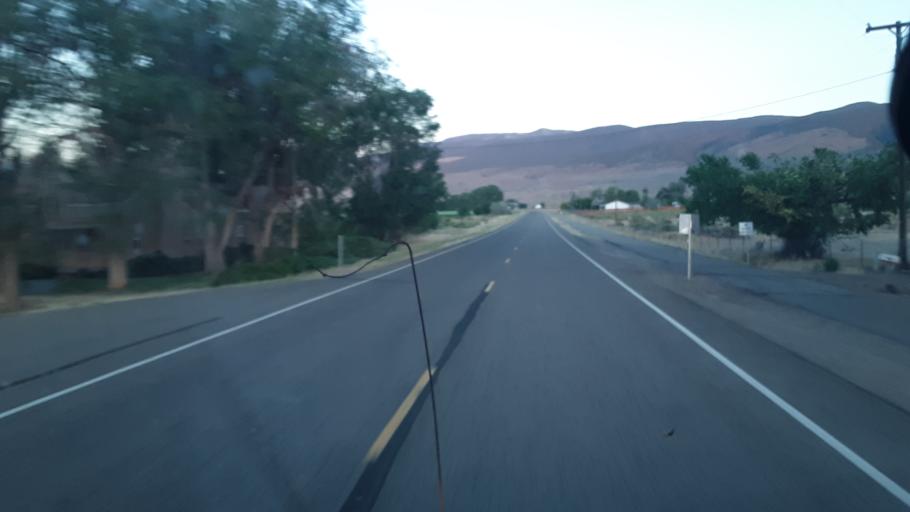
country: US
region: Utah
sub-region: Sevier County
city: Monroe
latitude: 38.6537
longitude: -112.1941
